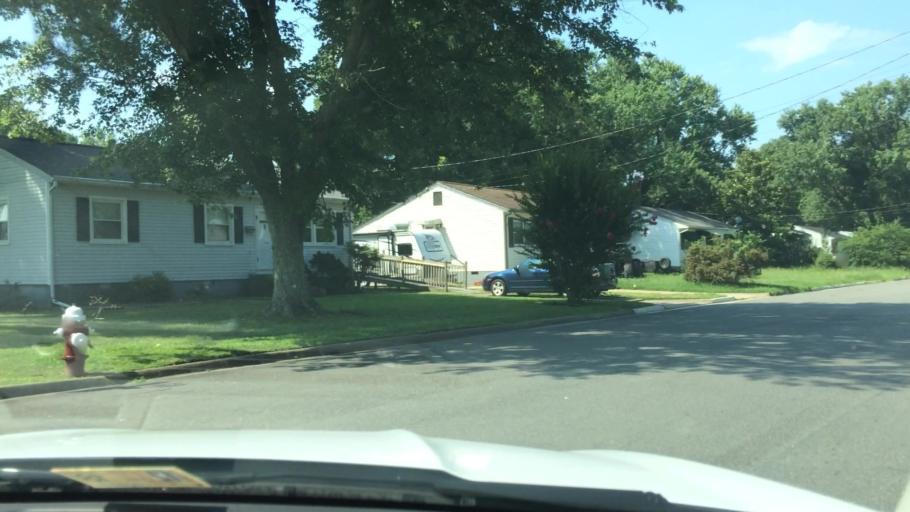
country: US
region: Virginia
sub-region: City of Newport News
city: Newport News
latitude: 37.0205
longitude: -76.4267
